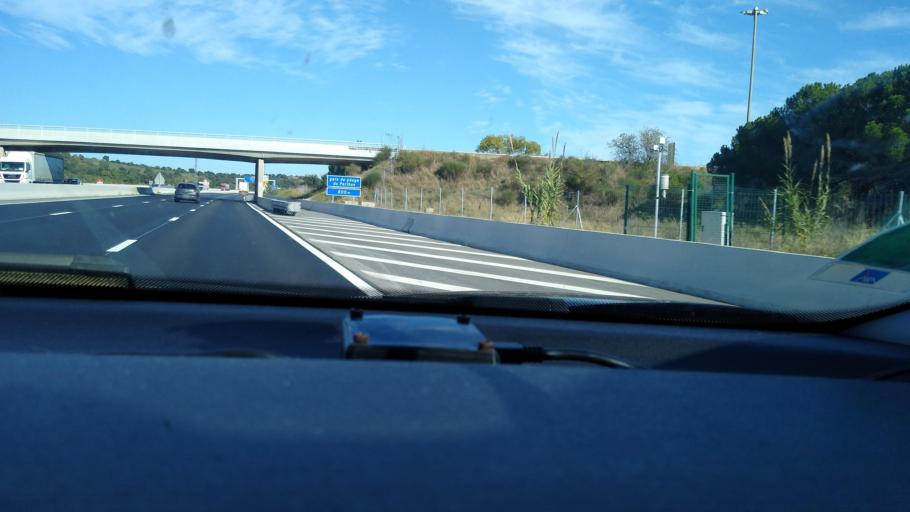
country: FR
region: Languedoc-Roussillon
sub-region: Departement des Pyrenees-Orientales
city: el Volo
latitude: 42.5201
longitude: 2.8191
